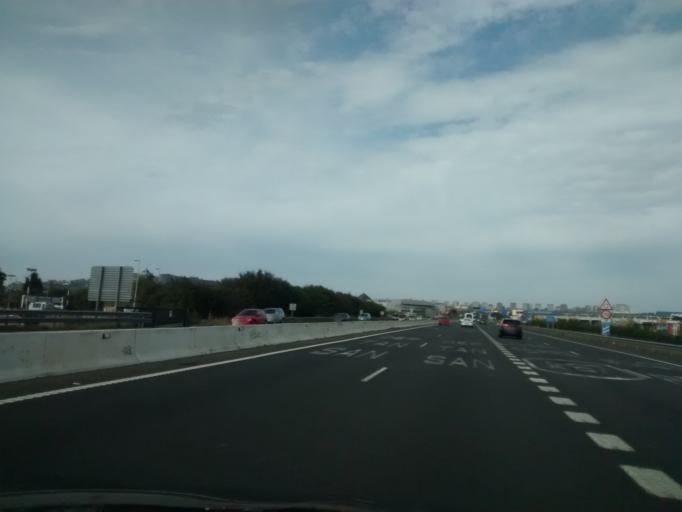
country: ES
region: Cantabria
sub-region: Provincia de Cantabria
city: El Astillero
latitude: 43.4296
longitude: -3.8363
